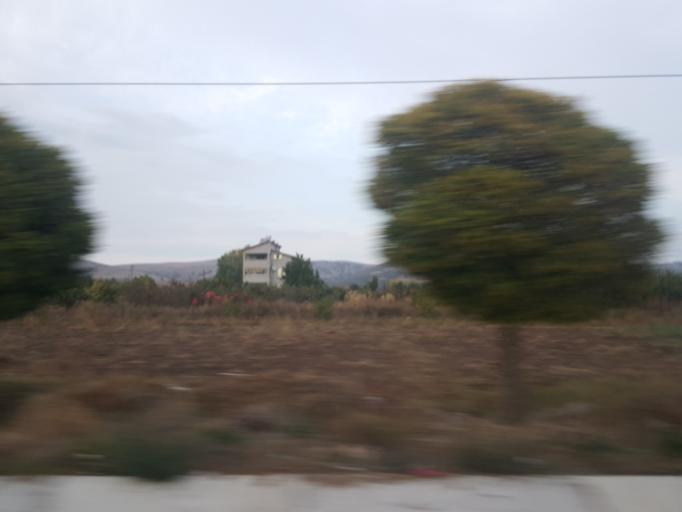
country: TR
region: Amasya
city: Gumushacikoy
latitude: 40.8853
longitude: 35.2099
